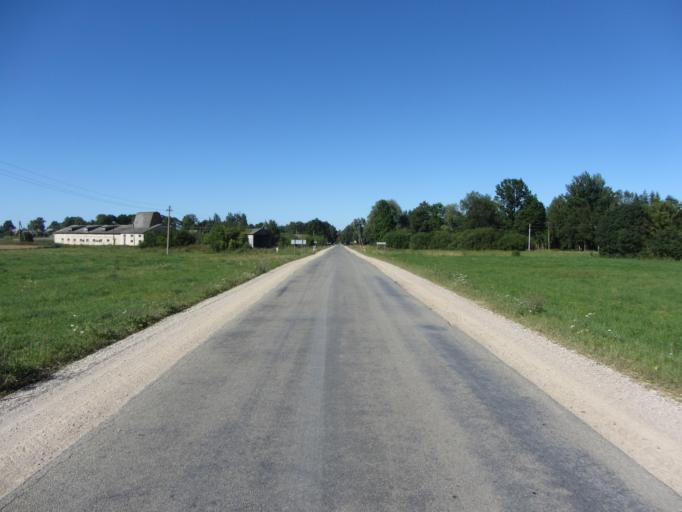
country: LT
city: Obeliai
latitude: 55.8849
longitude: 25.2000
